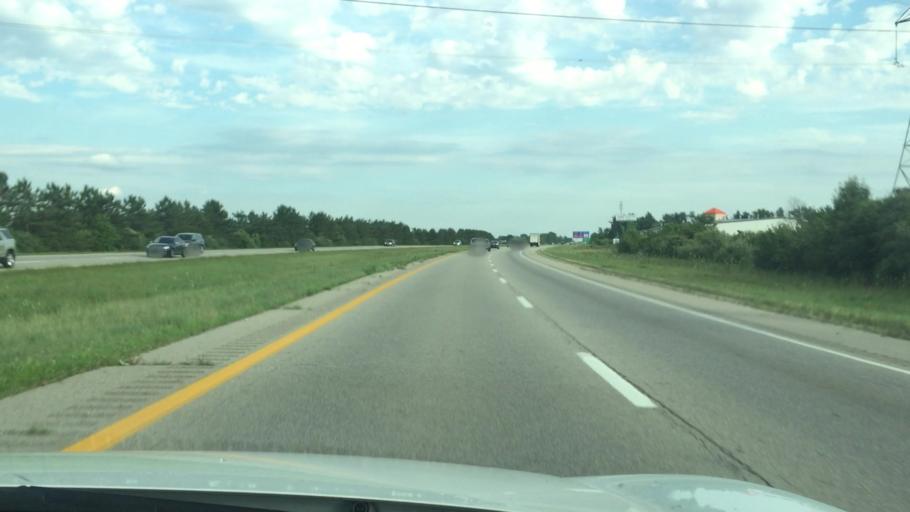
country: US
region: Ohio
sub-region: Union County
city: New California
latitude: 40.1265
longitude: -83.1887
